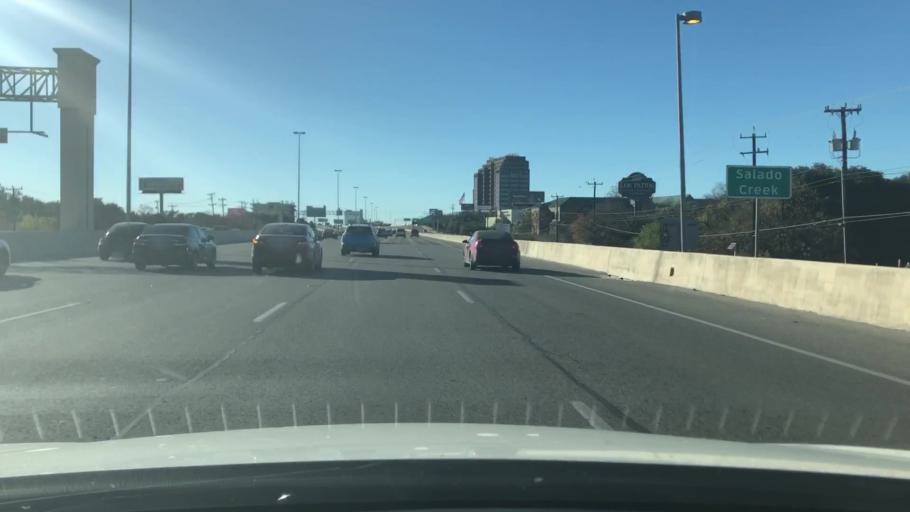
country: US
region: Texas
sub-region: Bexar County
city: Terrell Hills
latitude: 29.5165
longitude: -98.4285
